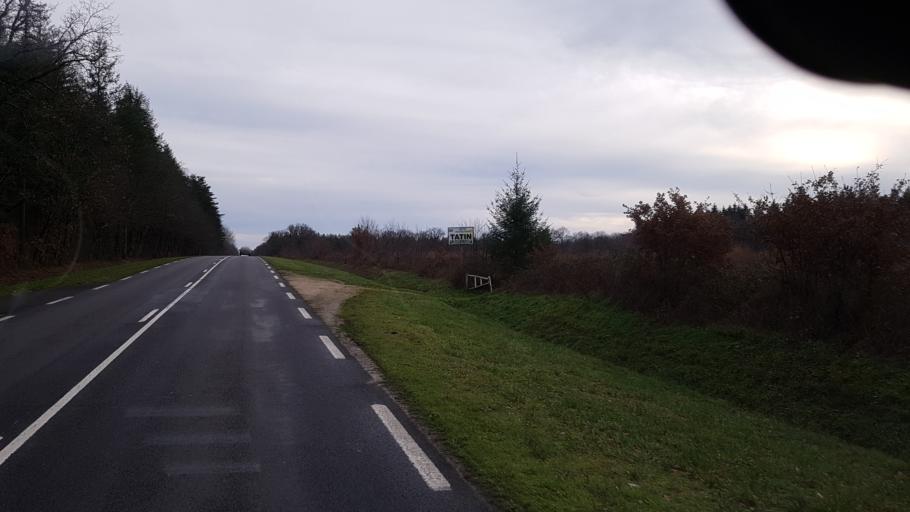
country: FR
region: Centre
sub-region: Departement du Loir-et-Cher
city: Lamotte-Beuvron
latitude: 47.6282
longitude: 2.0069
